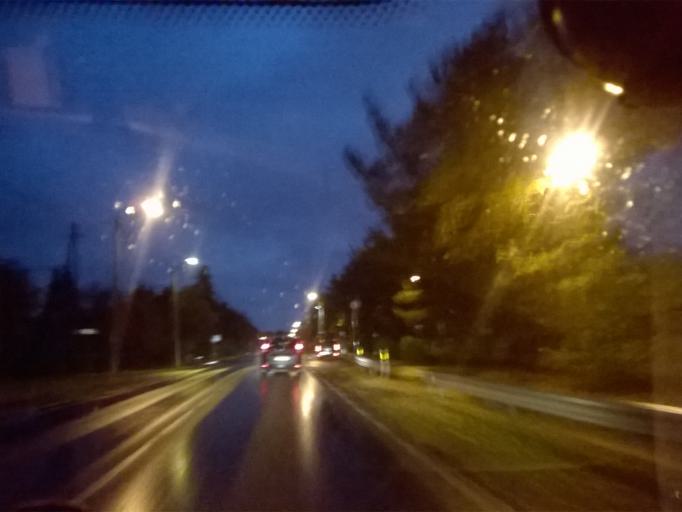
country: EE
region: Harju
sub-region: Viimsi vald
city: Viimsi
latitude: 59.4868
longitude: 24.8816
